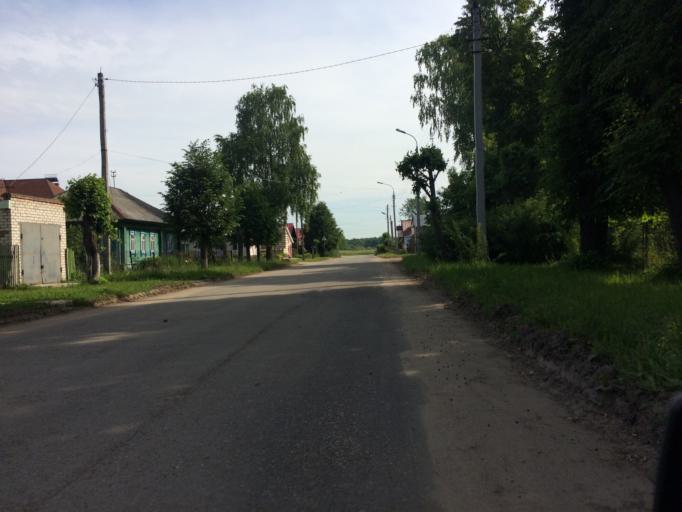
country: RU
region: Mariy-El
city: Yoshkar-Ola
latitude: 56.6513
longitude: 47.9146
